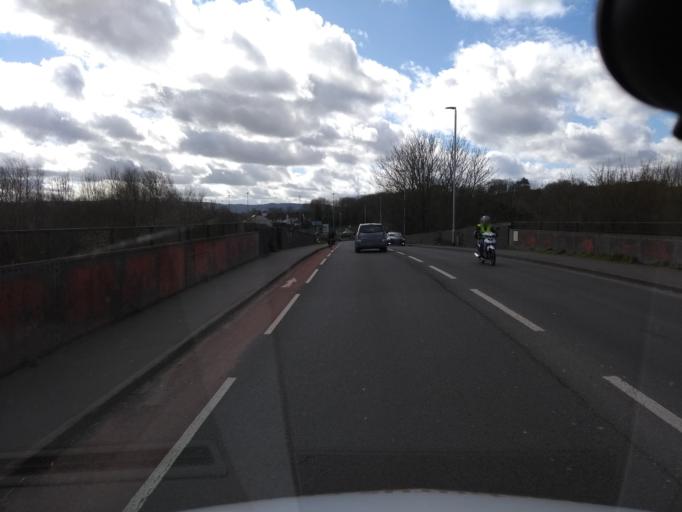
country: GB
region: England
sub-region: Somerset
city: Creech Saint Michael
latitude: 51.0264
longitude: -3.0703
